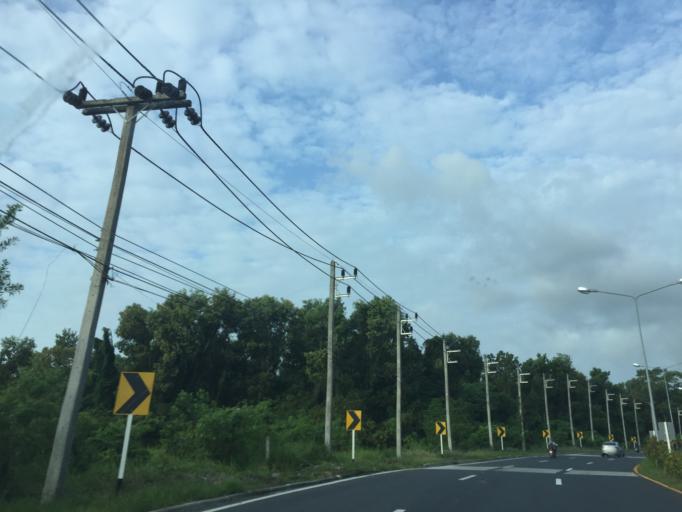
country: TH
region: Phuket
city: Mueang Phuket
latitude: 7.8828
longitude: 98.3598
